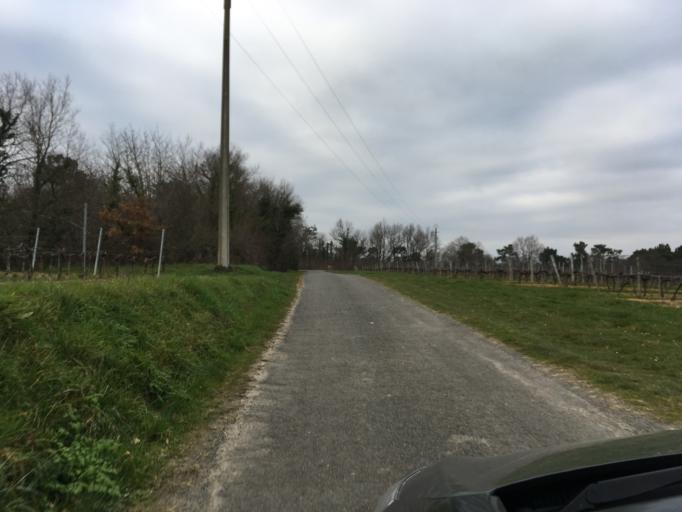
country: FR
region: Aquitaine
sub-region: Departement de la Gironde
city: Saint-Ciers-sur-Gironde
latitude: 45.3110
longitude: -0.6049
